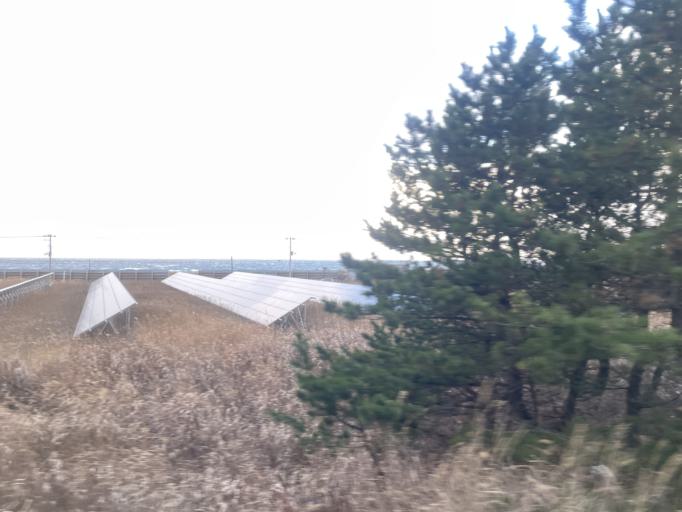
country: JP
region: Aomori
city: Mutsu
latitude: 41.0956
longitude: 141.2510
